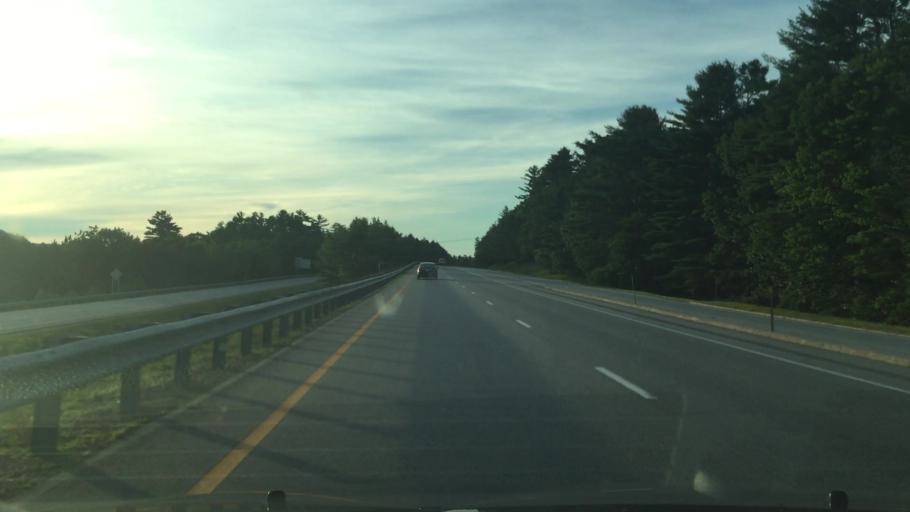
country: US
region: New Hampshire
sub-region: Grafton County
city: Ashland
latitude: 43.6995
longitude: -71.6469
